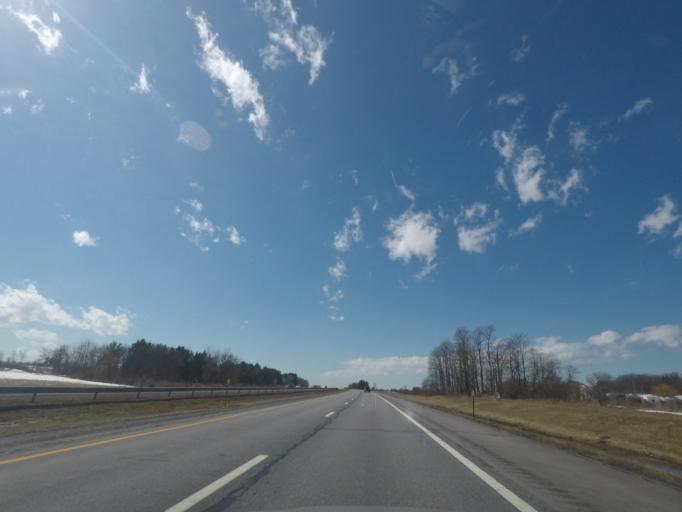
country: US
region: New York
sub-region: Montgomery County
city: Tribes Hill
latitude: 42.9335
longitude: -74.2484
